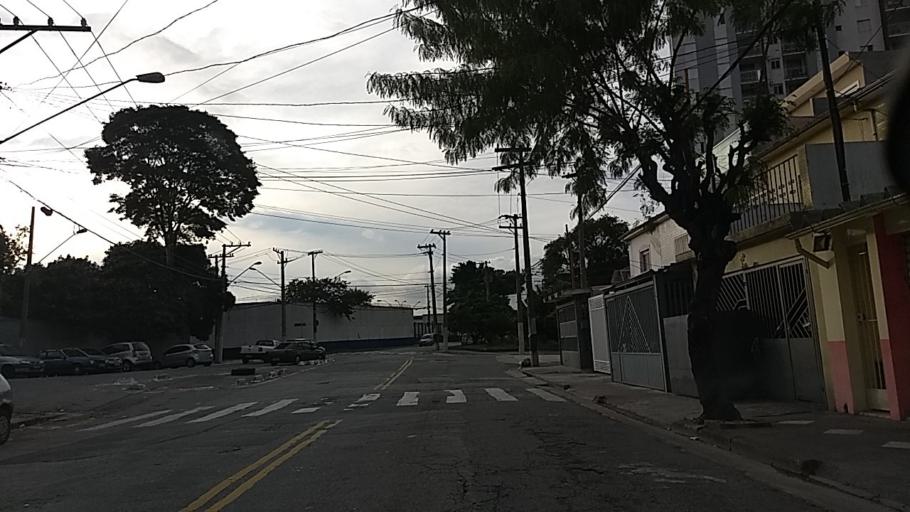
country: BR
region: Sao Paulo
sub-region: Sao Paulo
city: Sao Paulo
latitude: -23.5261
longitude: -46.6031
